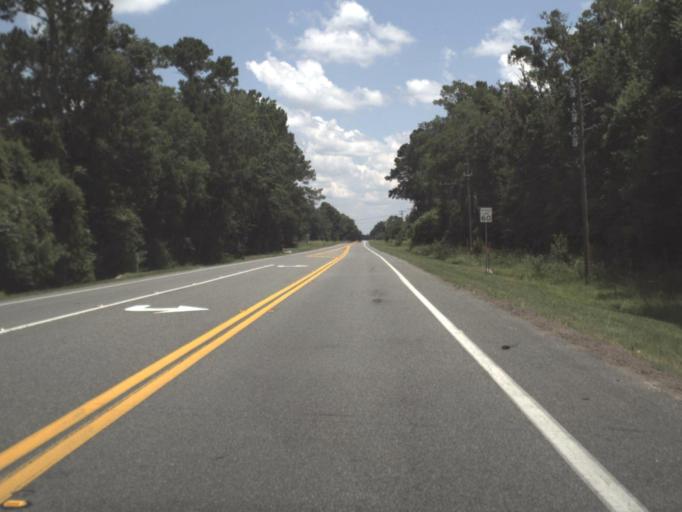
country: US
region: Florida
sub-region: Alachua County
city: Alachua
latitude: 29.8019
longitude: -82.3849
